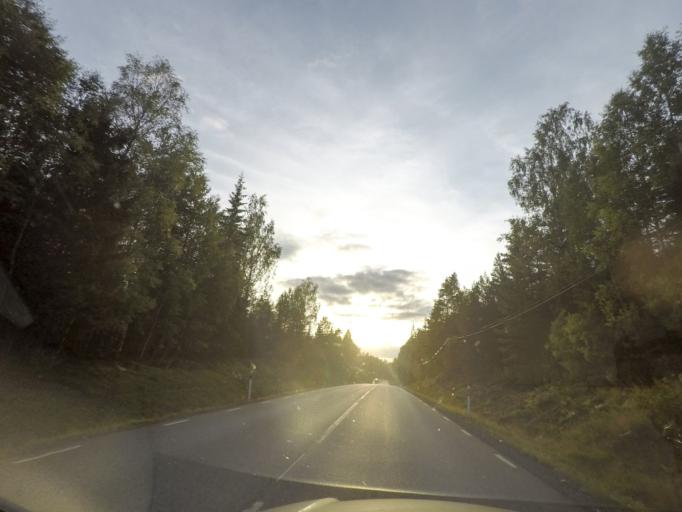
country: SE
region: OErebro
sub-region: Nora Kommun
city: As
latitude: 59.5445
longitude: 14.7764
